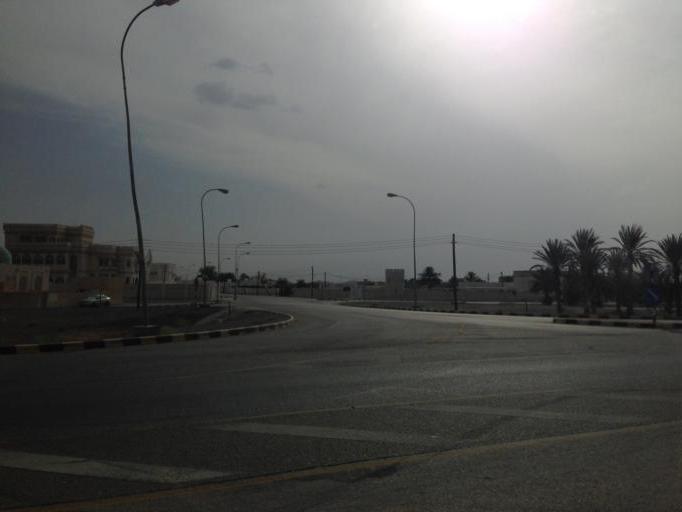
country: OM
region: Ash Sharqiyah
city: Al Qabil
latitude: 22.5731
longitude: 58.6955
